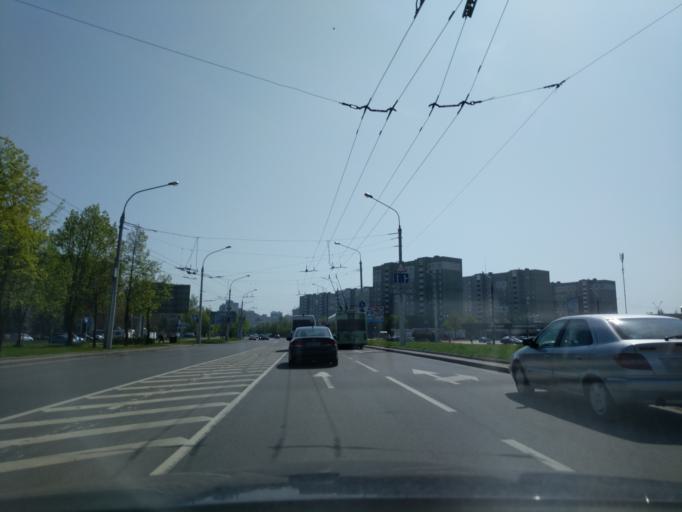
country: BY
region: Minsk
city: Malinovka
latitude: 53.8608
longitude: 27.4616
